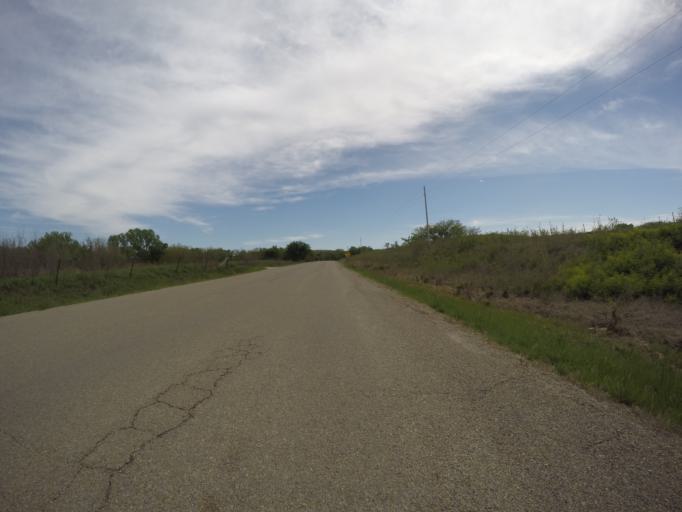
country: US
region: Kansas
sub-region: Riley County
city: Ogden
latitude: 39.0617
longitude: -96.6514
